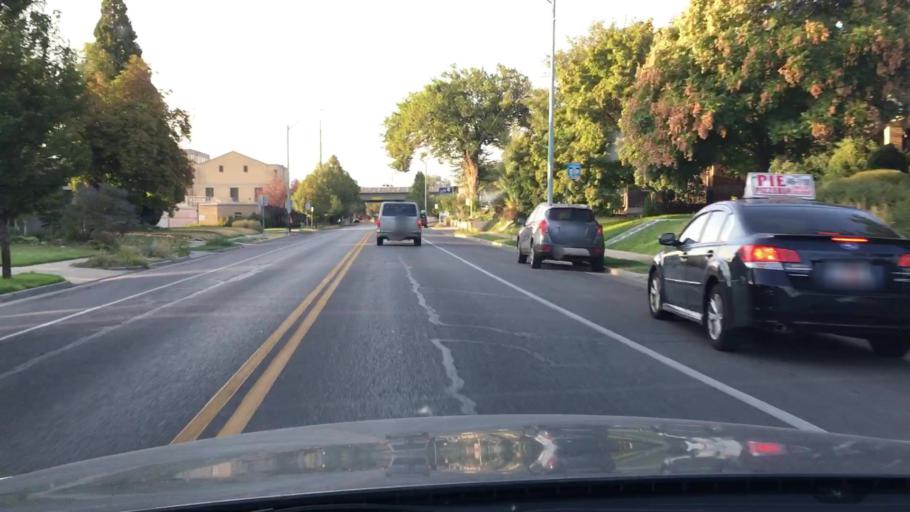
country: US
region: Utah
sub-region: Salt Lake County
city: Willard
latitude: 40.7175
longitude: -111.8566
